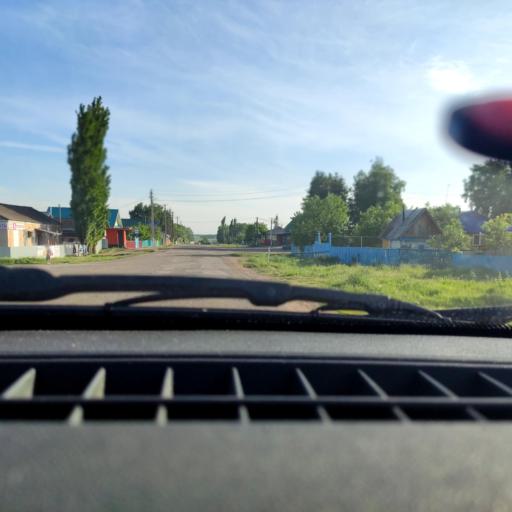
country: RU
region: Bashkortostan
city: Tolbazy
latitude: 54.2952
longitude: 55.8197
